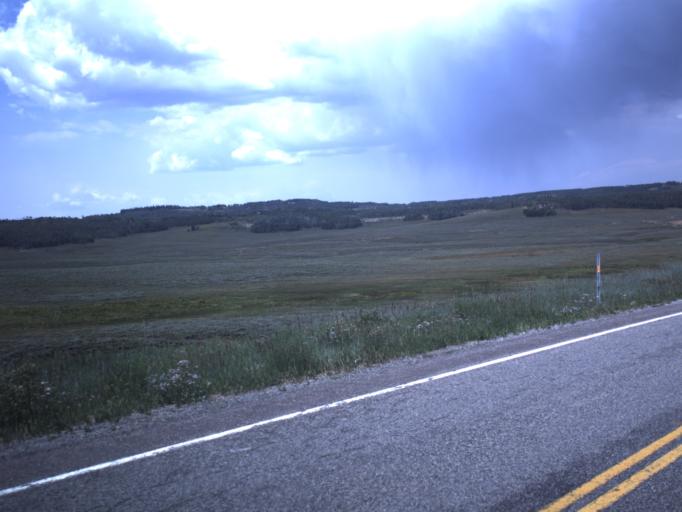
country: US
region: Utah
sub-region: Sanpete County
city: Fairview
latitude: 39.6582
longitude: -111.3007
